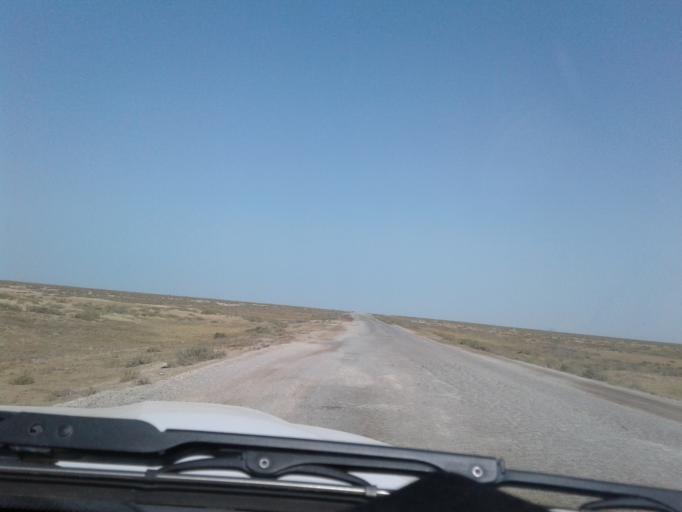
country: IR
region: Golestan
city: Gomishan
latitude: 37.8960
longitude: 53.8671
